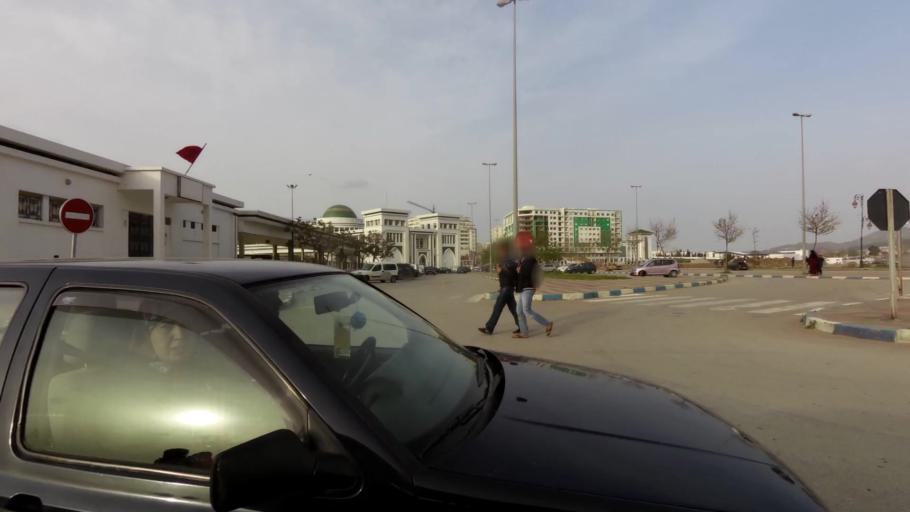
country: MA
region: Tanger-Tetouan
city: Tetouan
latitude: 35.5598
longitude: -5.3723
